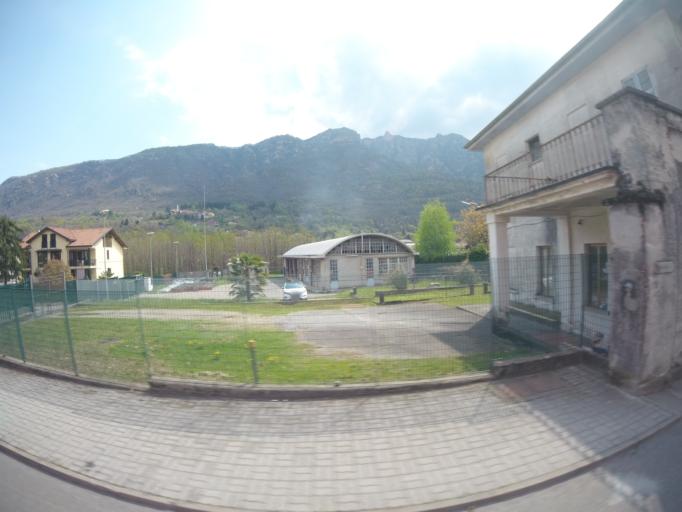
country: IT
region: Piedmont
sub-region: Provincia Verbano-Cusio-Ossola
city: Gabbio-Cereda-Ramate
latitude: 45.9014
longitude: 8.4173
